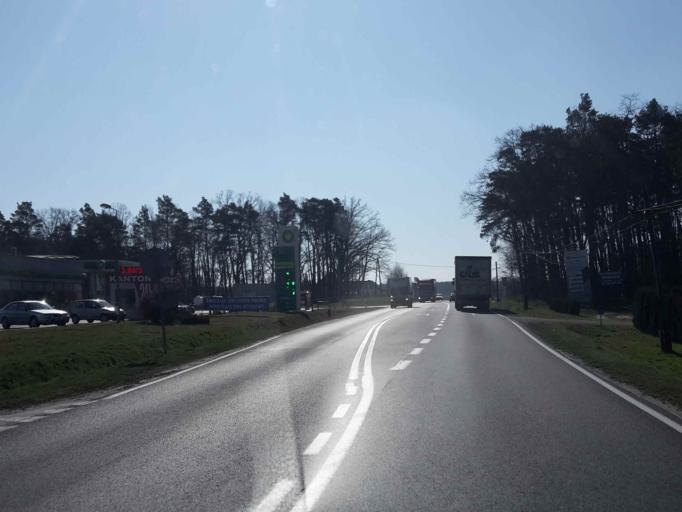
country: PL
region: Greater Poland Voivodeship
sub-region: Powiat nowotomyski
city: Nowy Tomysl
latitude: 52.3395
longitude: 16.1076
